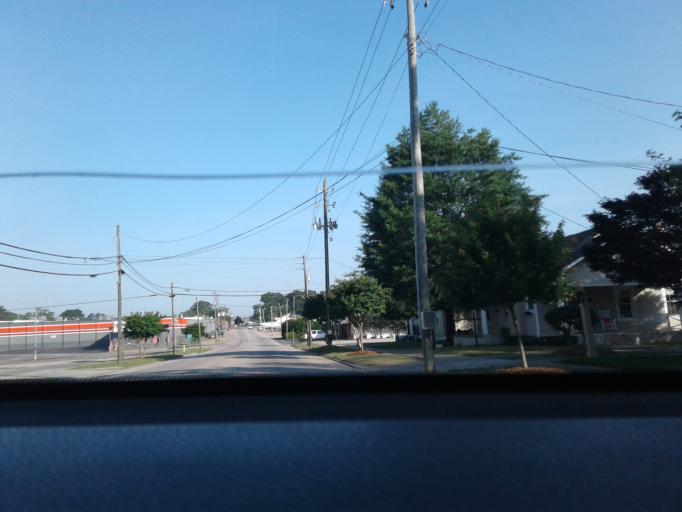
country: US
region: North Carolina
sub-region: Harnett County
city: Dunn
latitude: 35.3120
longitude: -78.6167
